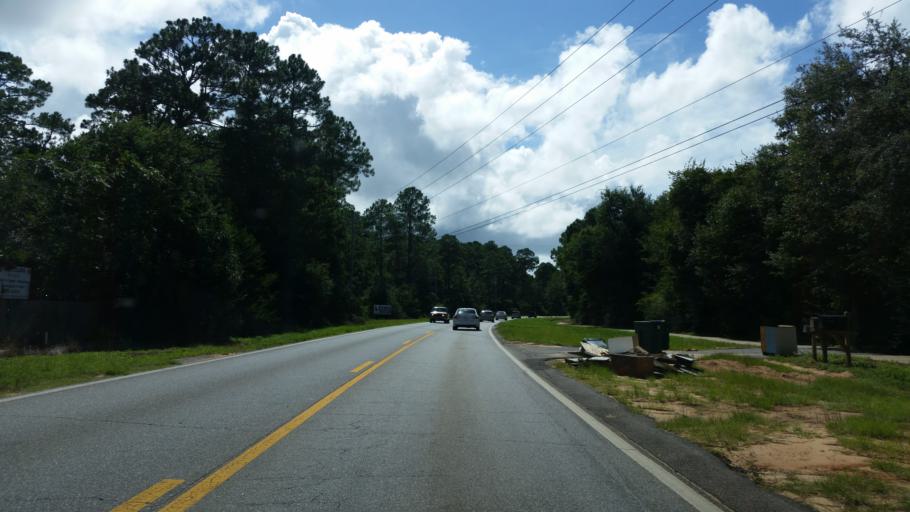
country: US
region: Florida
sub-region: Santa Rosa County
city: Holley
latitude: 30.4330
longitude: -86.9083
